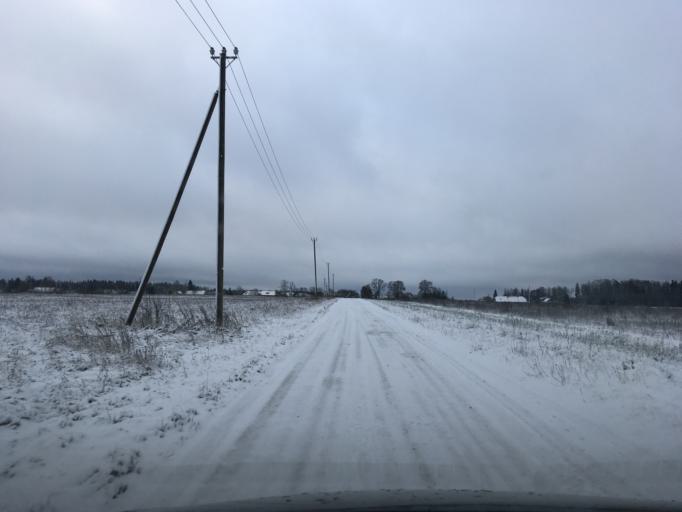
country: EE
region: Harju
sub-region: Raasiku vald
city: Raasiku
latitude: 59.2156
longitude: 25.1941
